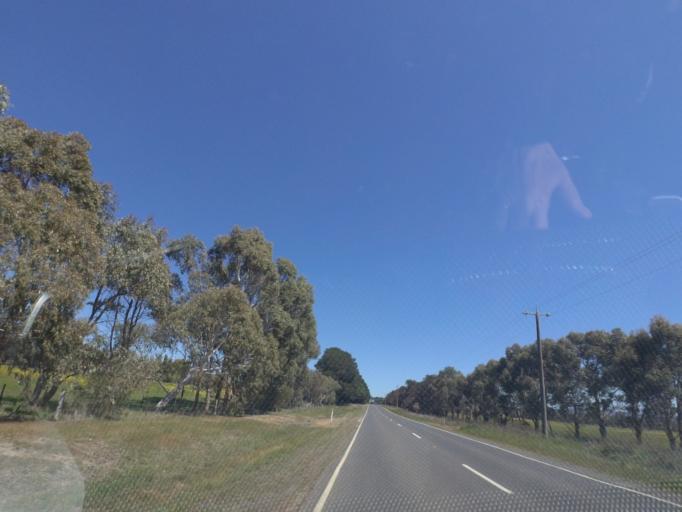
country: AU
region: Victoria
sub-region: Hume
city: Sunbury
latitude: -37.2850
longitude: 144.7661
